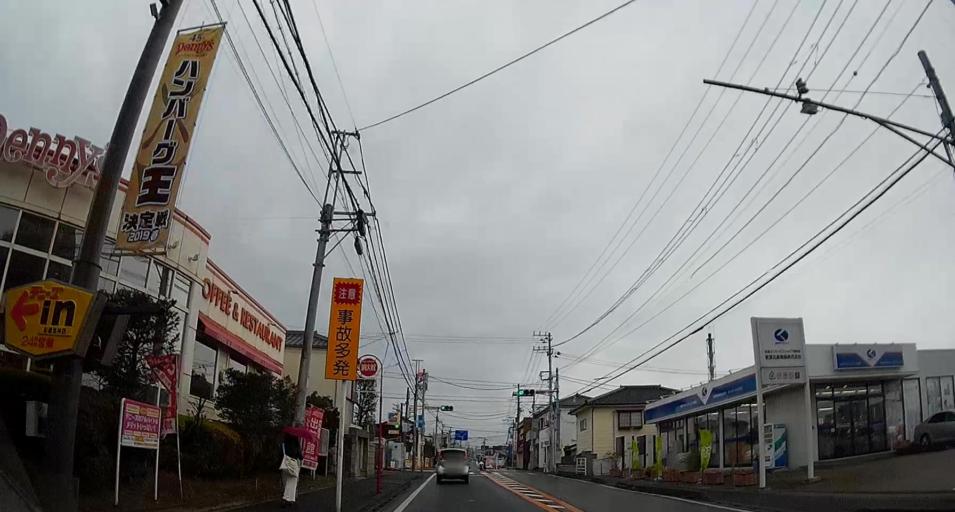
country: JP
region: Chiba
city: Funabashi
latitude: 35.7041
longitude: 139.9718
